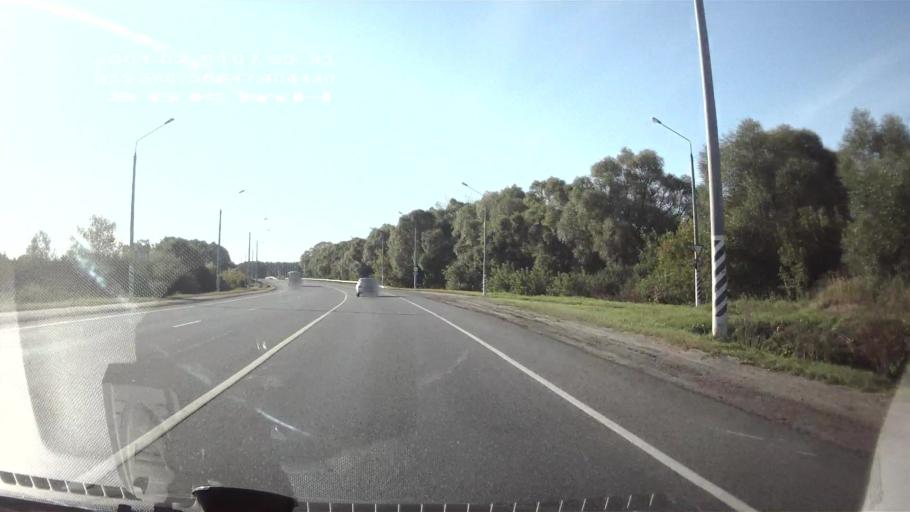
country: RU
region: Chuvashia
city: Shikhazany
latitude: 55.5605
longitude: 47.4047
